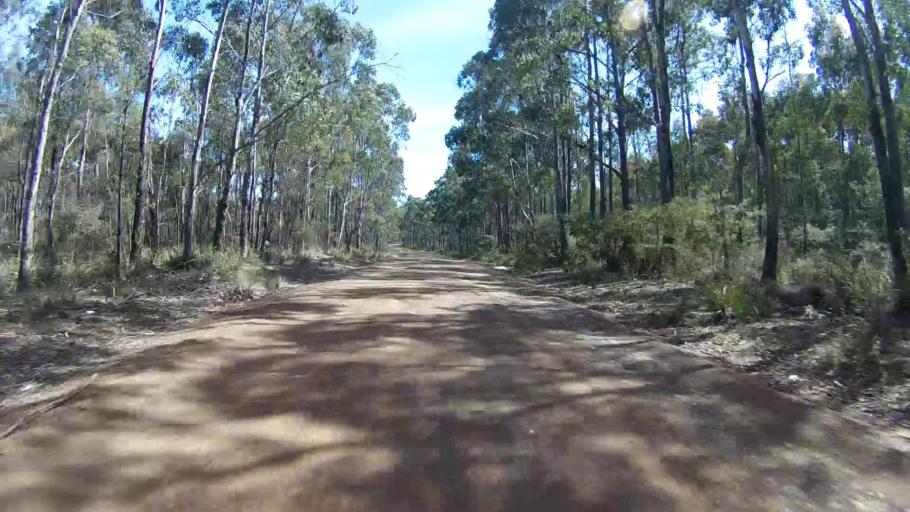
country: AU
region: Tasmania
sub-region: Sorell
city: Sorell
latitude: -42.6800
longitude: 147.7312
